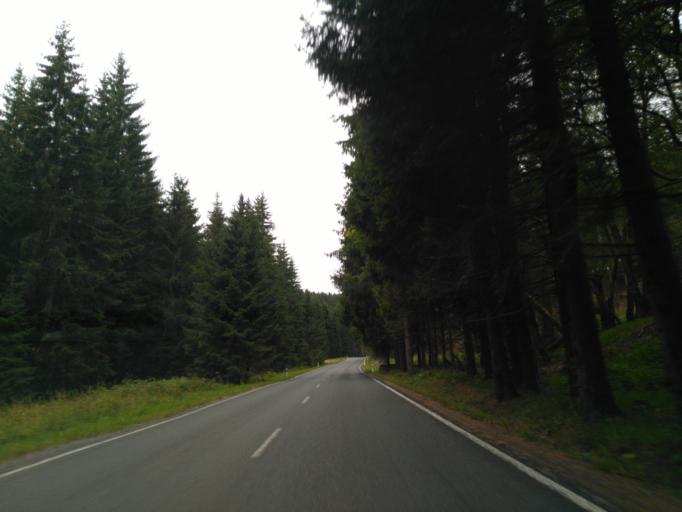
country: DE
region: Saxony
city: Johanngeorgenstadt
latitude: 50.3982
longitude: 12.7491
